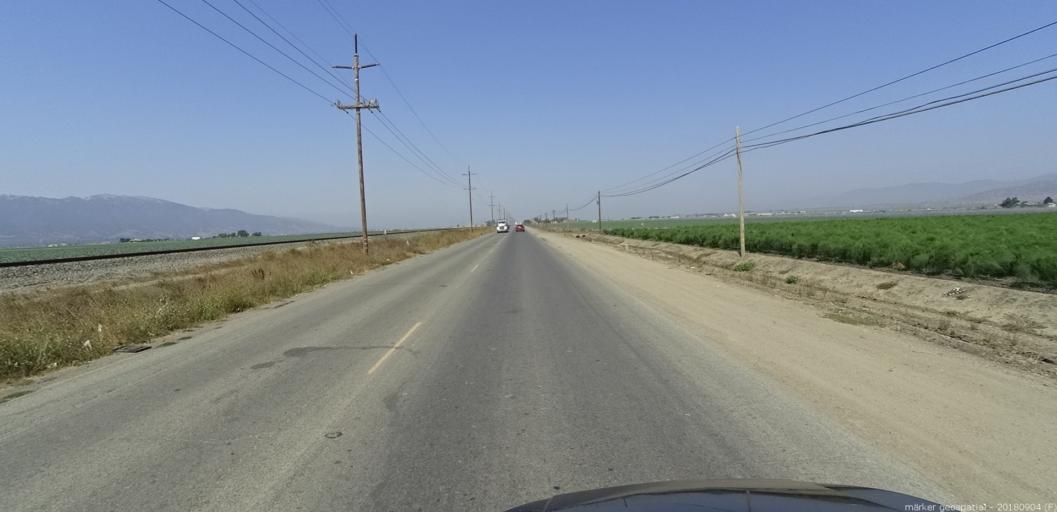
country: US
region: California
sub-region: Monterey County
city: Gonzales
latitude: 36.5133
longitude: -121.4534
